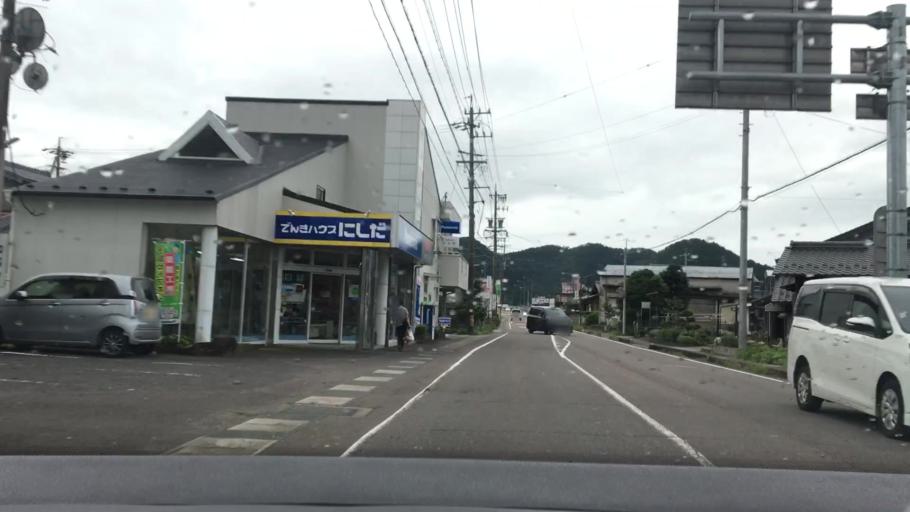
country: JP
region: Gifu
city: Mino
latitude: 35.5199
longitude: 136.8558
